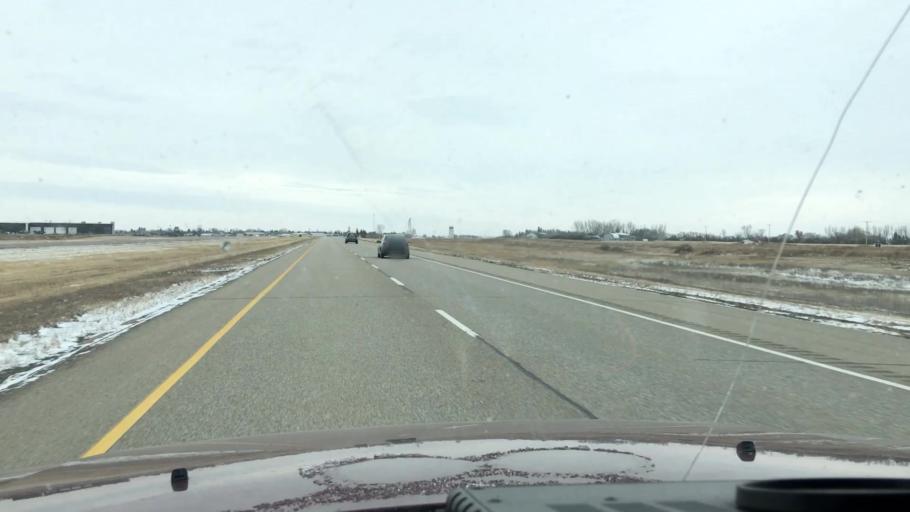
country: CA
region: Saskatchewan
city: Watrous
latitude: 51.2785
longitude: -106.0131
